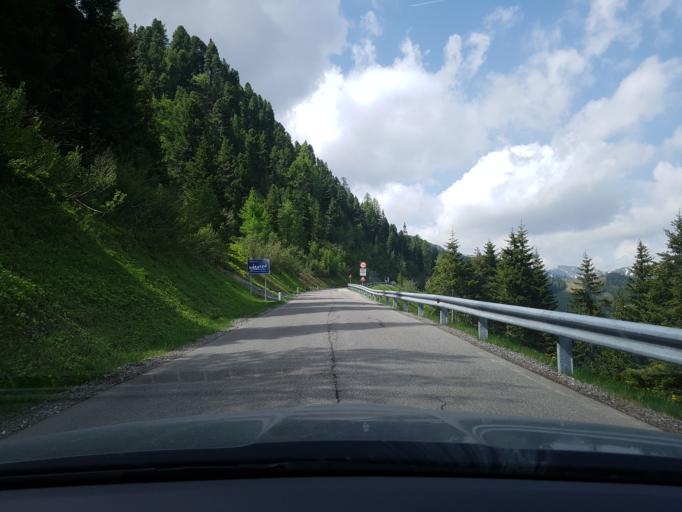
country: AT
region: Salzburg
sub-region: Politischer Bezirk Tamsweg
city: Thomatal
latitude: 46.9758
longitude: 13.7706
